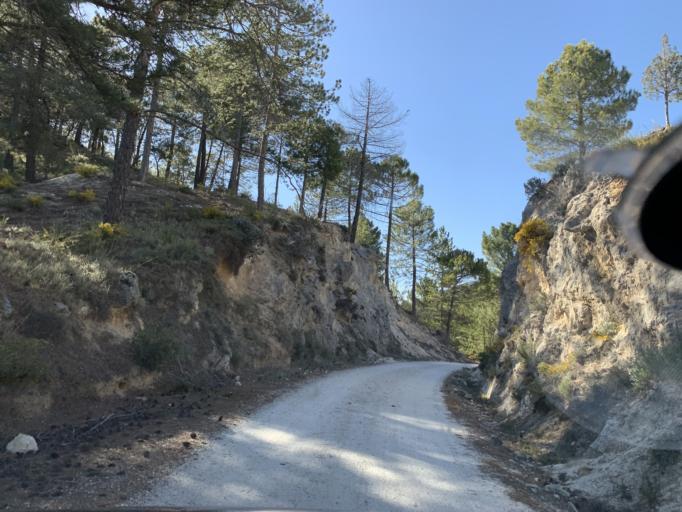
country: ES
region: Andalusia
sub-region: Provincia de Granada
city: Beas de Granada
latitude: 37.2509
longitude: -3.4636
